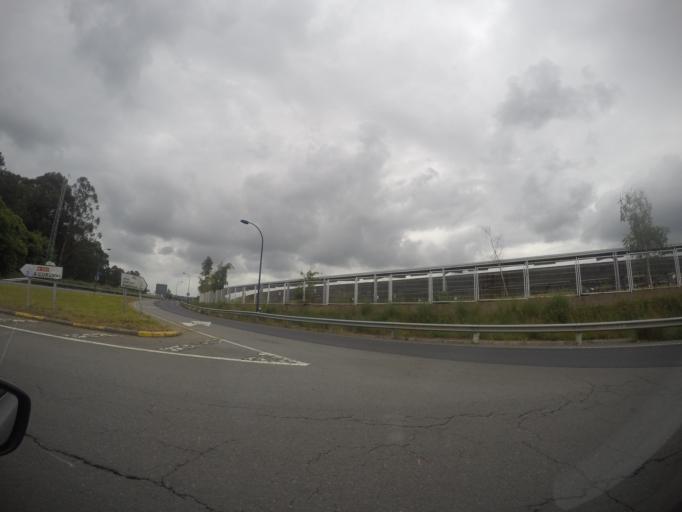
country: ES
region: Galicia
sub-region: Provincia da Coruna
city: Culleredo
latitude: 43.3080
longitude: -8.3759
